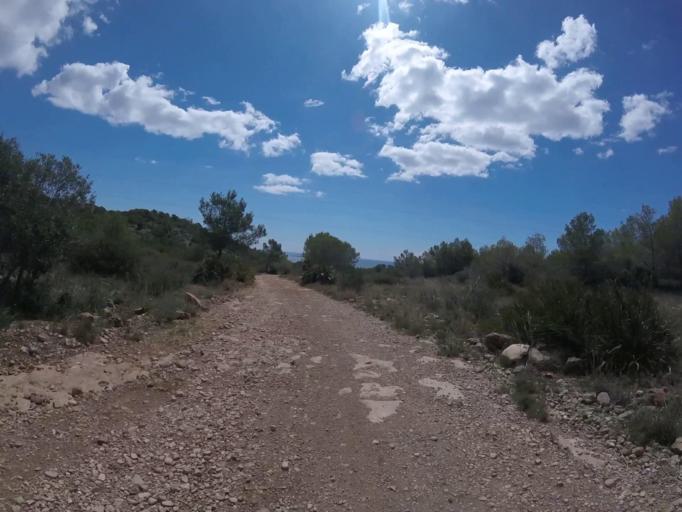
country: ES
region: Valencia
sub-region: Provincia de Castello
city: Alcoceber
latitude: 40.2897
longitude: 0.3172
